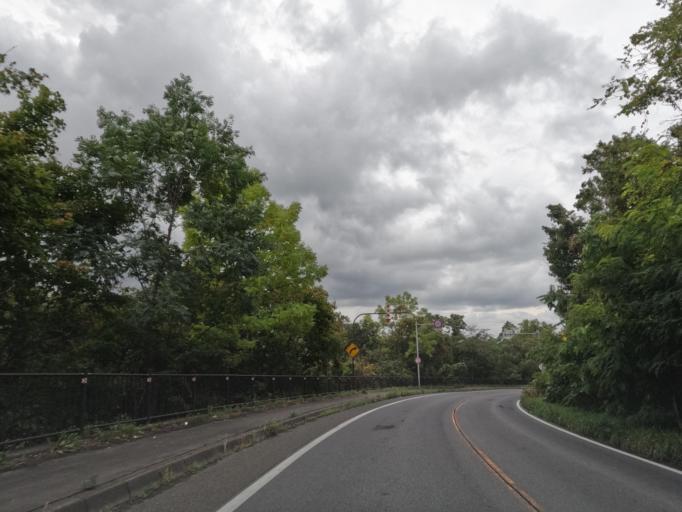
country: JP
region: Hokkaido
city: Date
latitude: 42.5254
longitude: 140.8625
